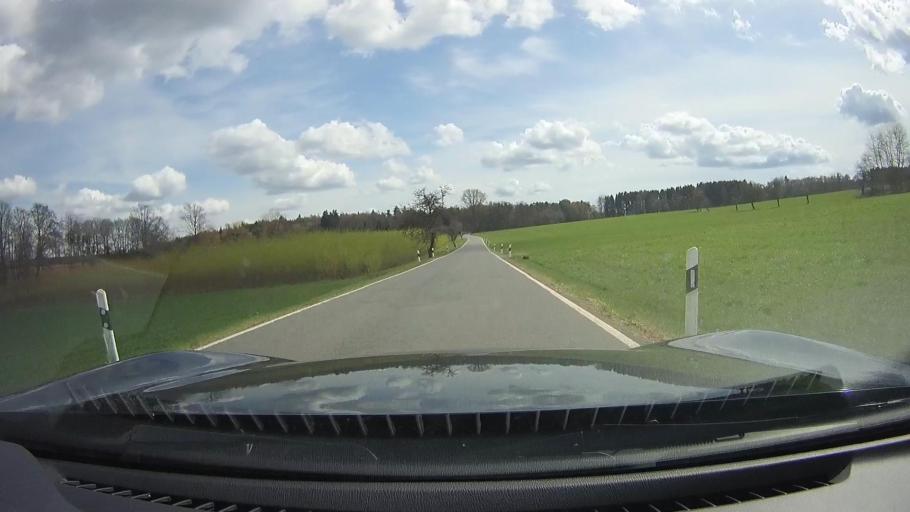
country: DE
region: Hesse
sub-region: Regierungsbezirk Darmstadt
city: Hesseneck
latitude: 49.6311
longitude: 9.0991
